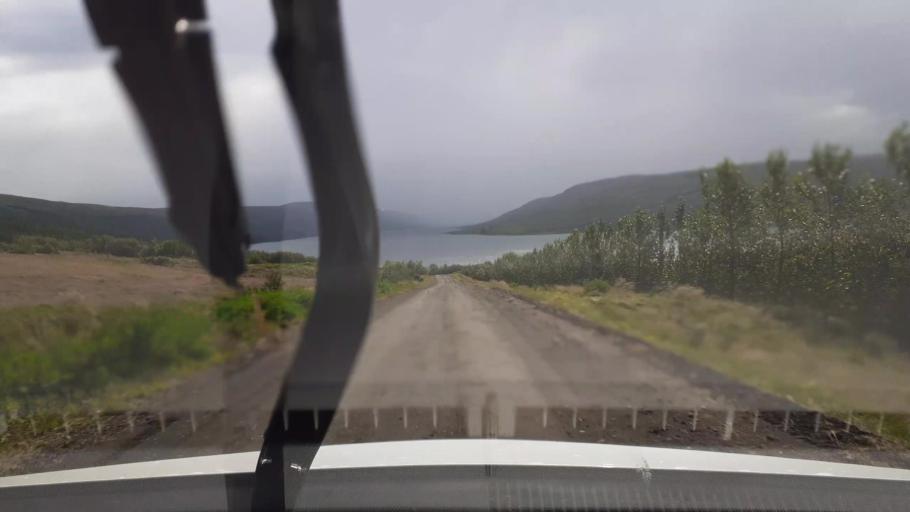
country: IS
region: Capital Region
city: Mosfellsbaer
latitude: 64.5234
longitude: -21.4714
